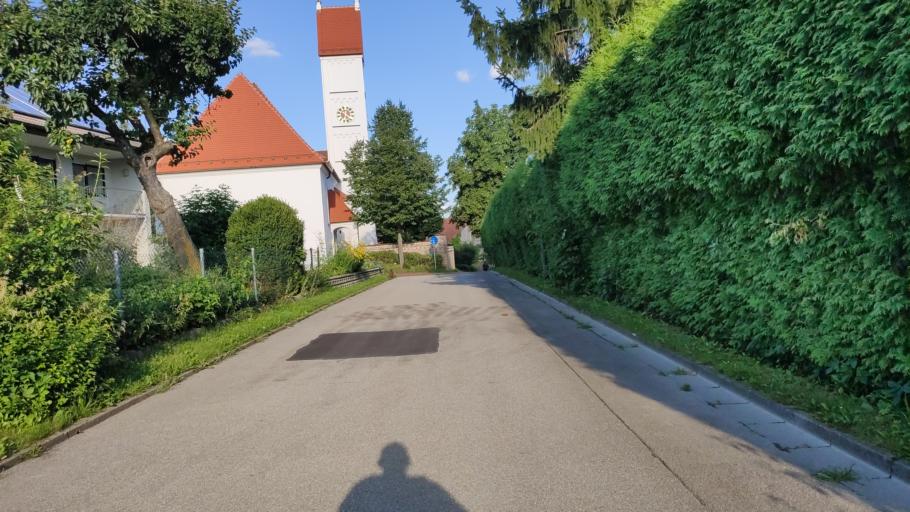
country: DE
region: Bavaria
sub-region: Swabia
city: Oberottmarshausen
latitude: 48.2377
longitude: 10.8557
